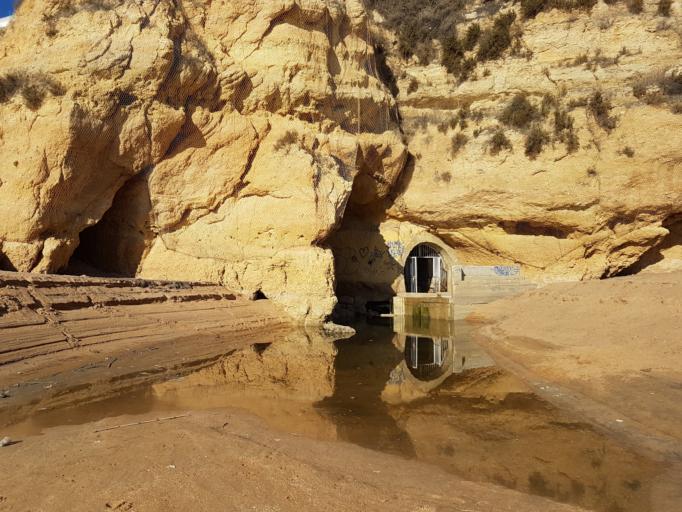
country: PT
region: Faro
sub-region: Albufeira
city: Albufeira
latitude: 37.0864
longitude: -8.2515
